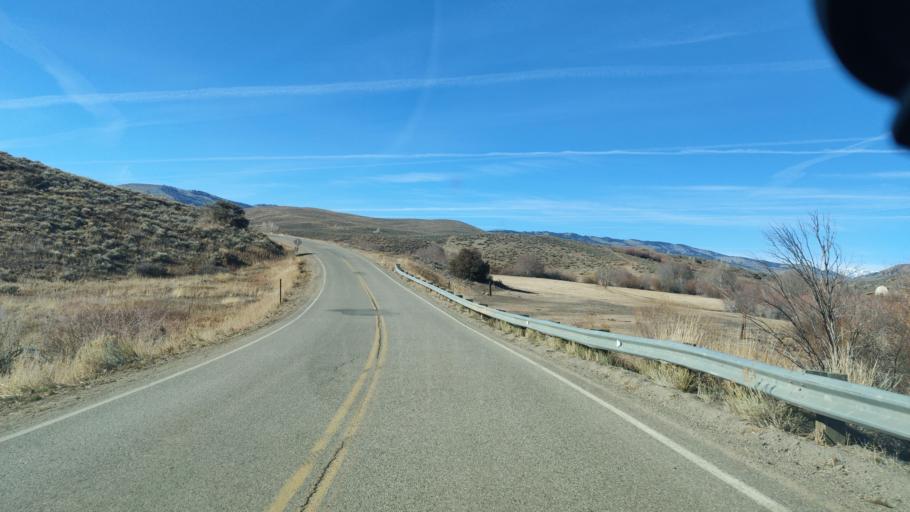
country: US
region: Colorado
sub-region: Gunnison County
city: Gunnison
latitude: 38.5776
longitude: -106.9622
